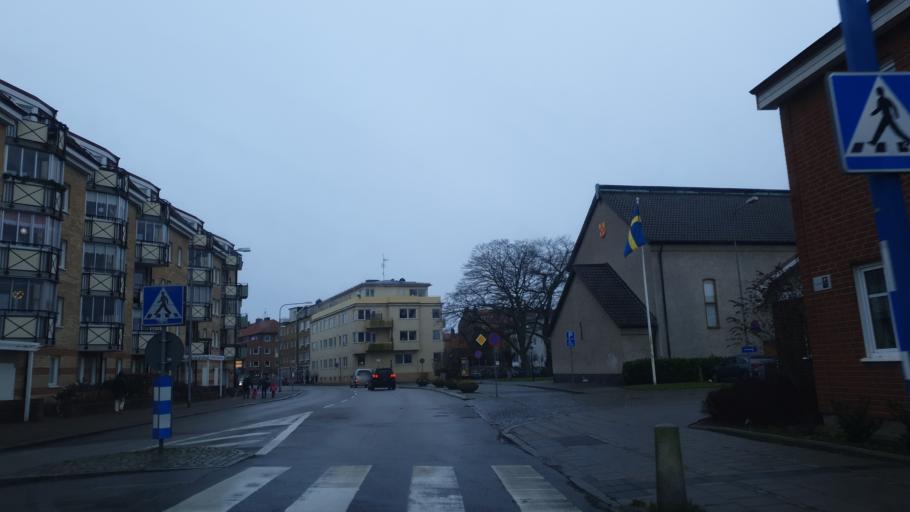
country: SE
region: Skane
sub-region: Trelleborgs Kommun
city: Trelleborg
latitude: 55.3761
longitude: 13.1536
